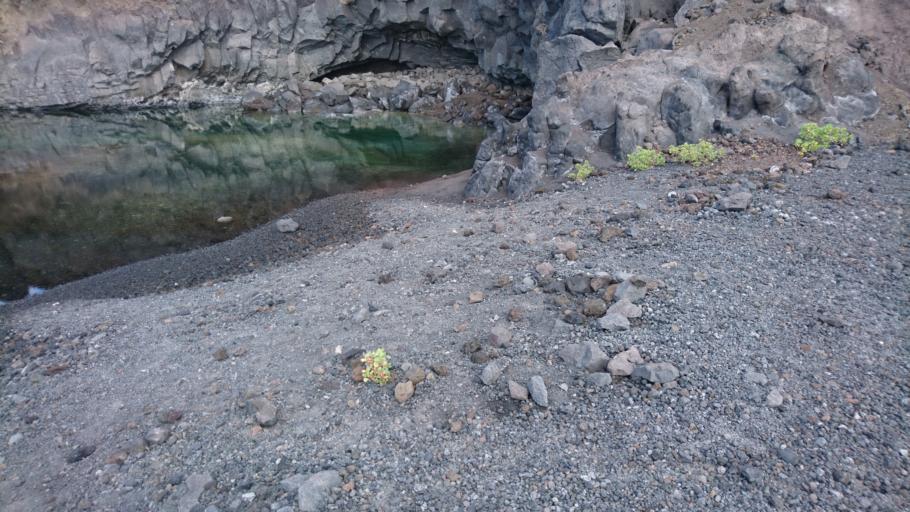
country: ES
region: Canary Islands
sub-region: Provincia de Santa Cruz de Tenerife
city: Fuencaliente de la Palma
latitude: 28.4597
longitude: -17.8513
